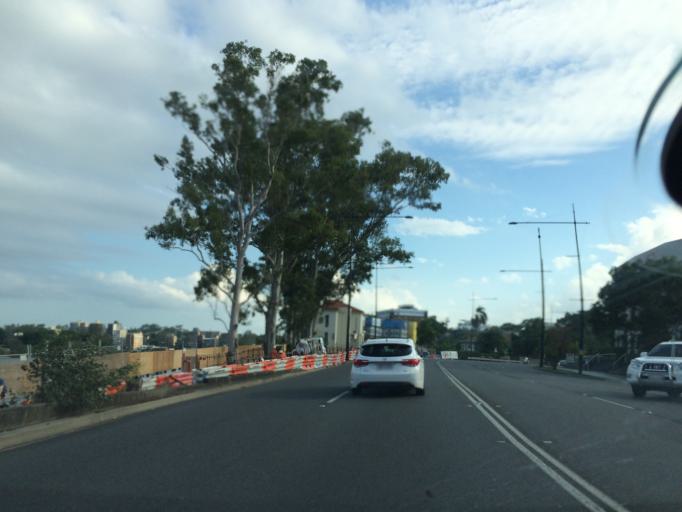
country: AU
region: Queensland
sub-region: Brisbane
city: Toowong
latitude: -27.4827
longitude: 152.9966
